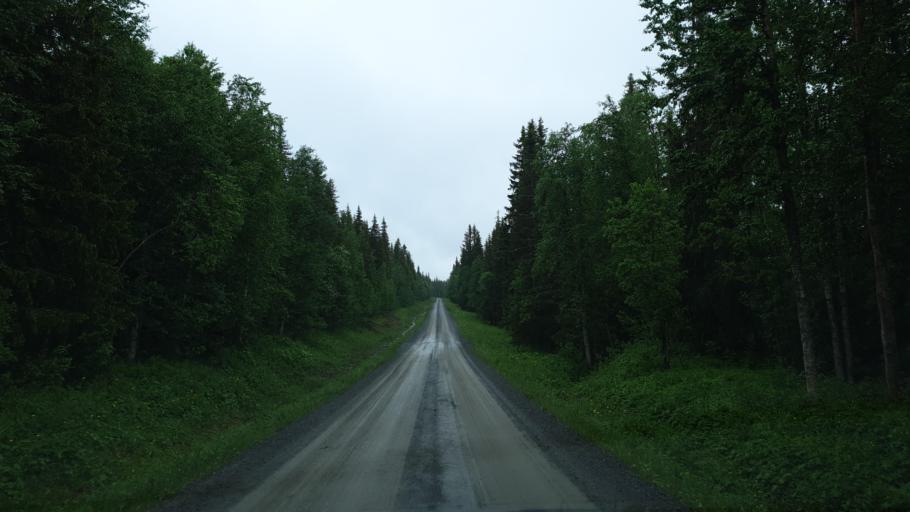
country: SE
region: Vaesterbotten
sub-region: Vilhelmina Kommun
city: Sjoberg
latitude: 65.3429
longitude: 15.8805
